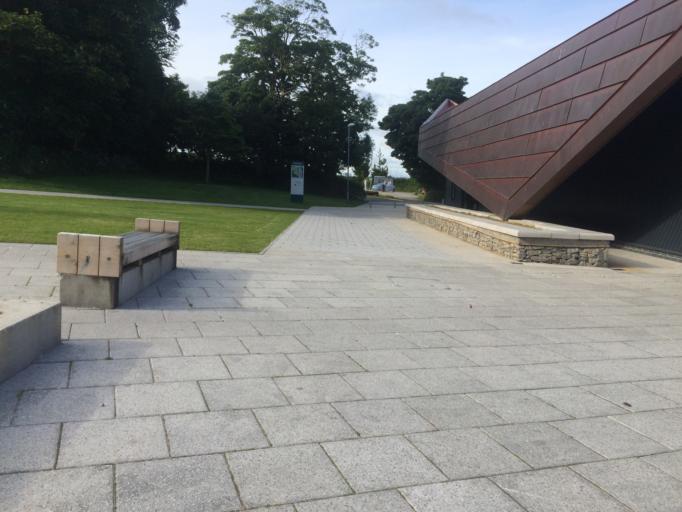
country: GB
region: England
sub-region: Cornwall
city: Penryn
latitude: 50.1710
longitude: -5.1236
